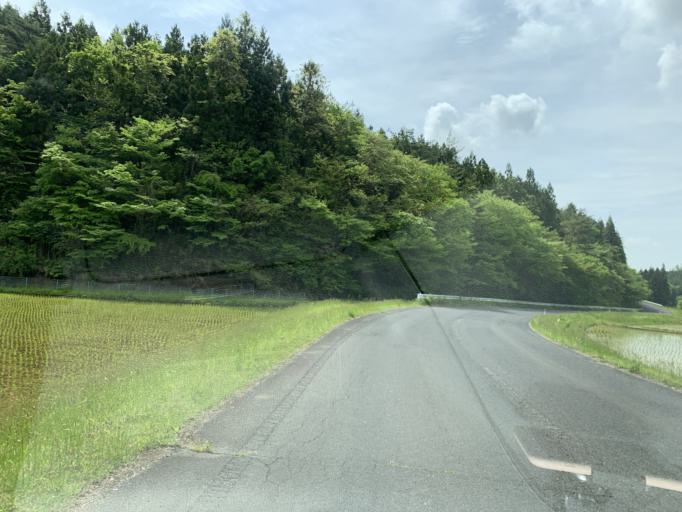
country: JP
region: Iwate
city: Ichinoseki
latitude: 38.8805
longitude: 140.9751
